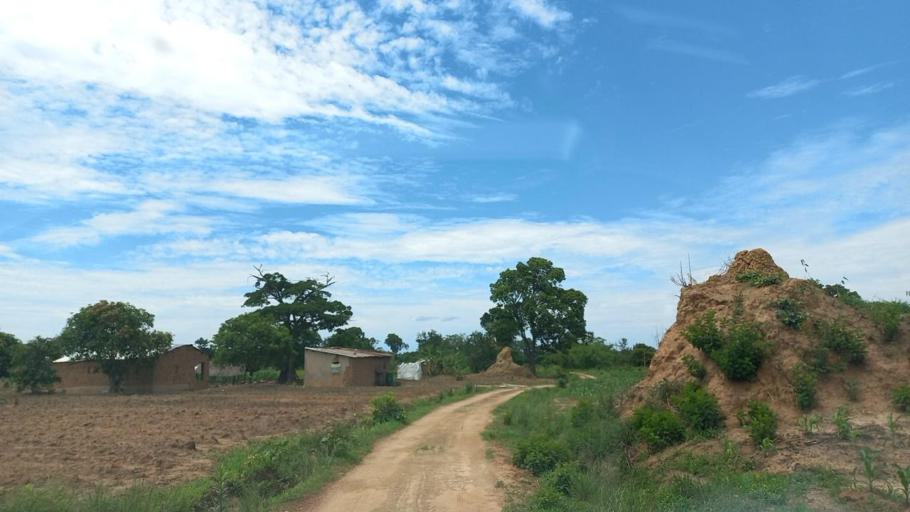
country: ZM
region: Copperbelt
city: Kitwe
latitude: -12.8117
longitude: 28.3970
